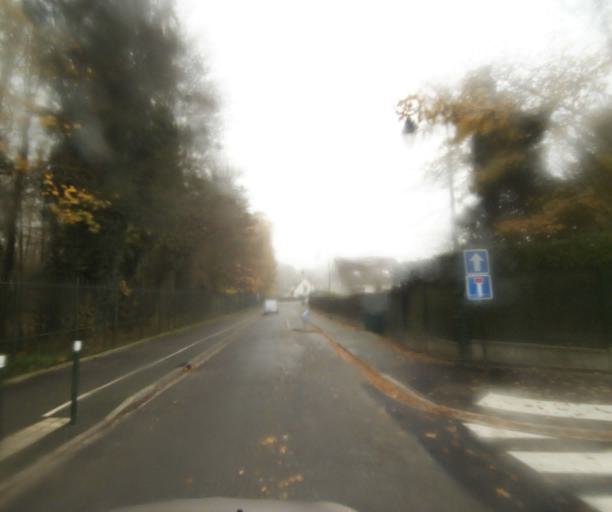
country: FR
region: Ile-de-France
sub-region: Departement de Seine-Saint-Denis
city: Tremblay-en-France
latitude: 48.9410
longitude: 2.5673
